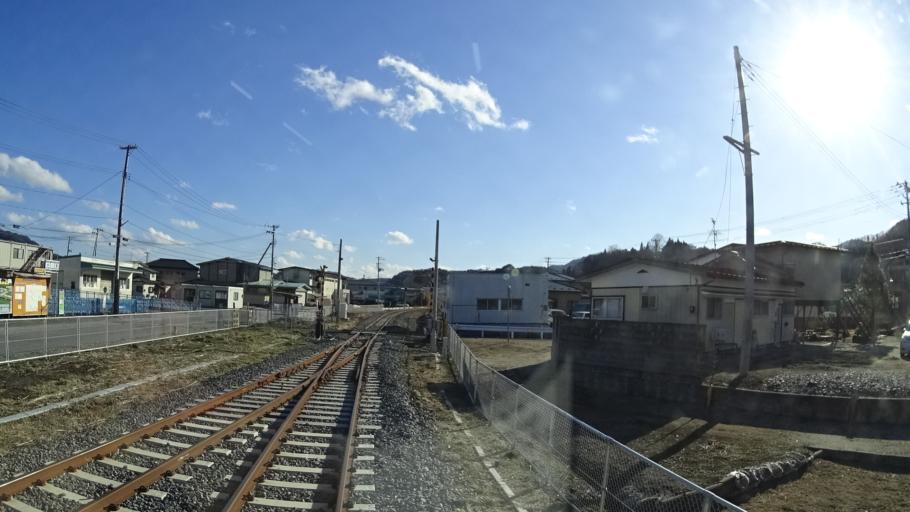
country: JP
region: Iwate
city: Miyako
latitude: 39.5801
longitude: 141.9369
